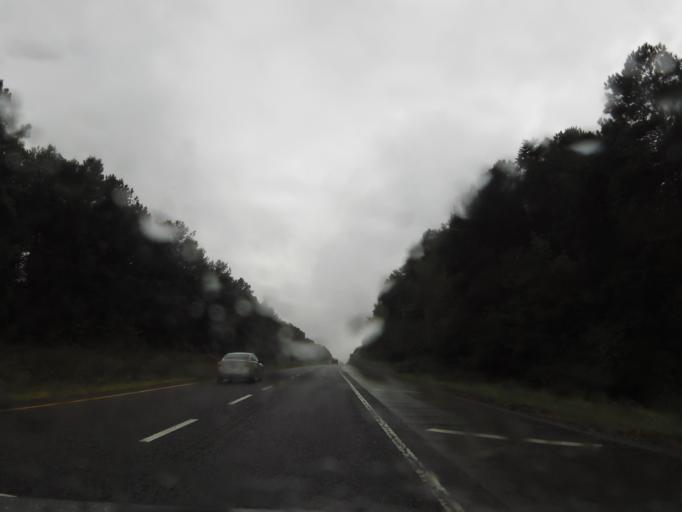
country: US
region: Tennessee
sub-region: Bradley County
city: Hopewell
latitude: 35.2801
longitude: -84.8196
